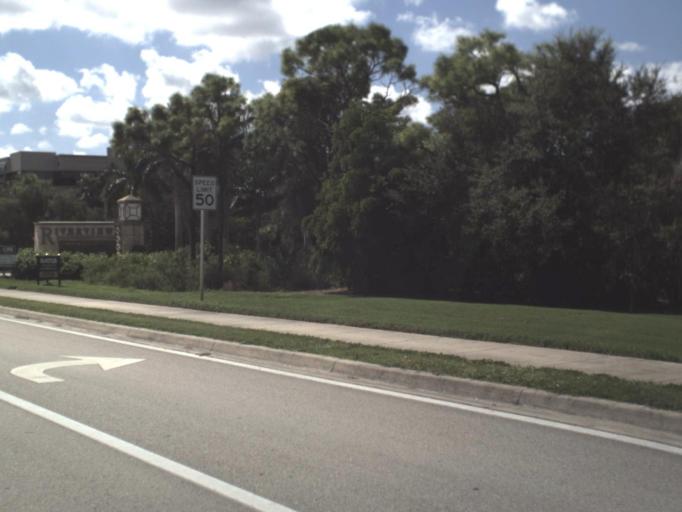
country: US
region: Florida
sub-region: Lee County
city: Bonita Springs
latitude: 26.3441
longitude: -81.8073
